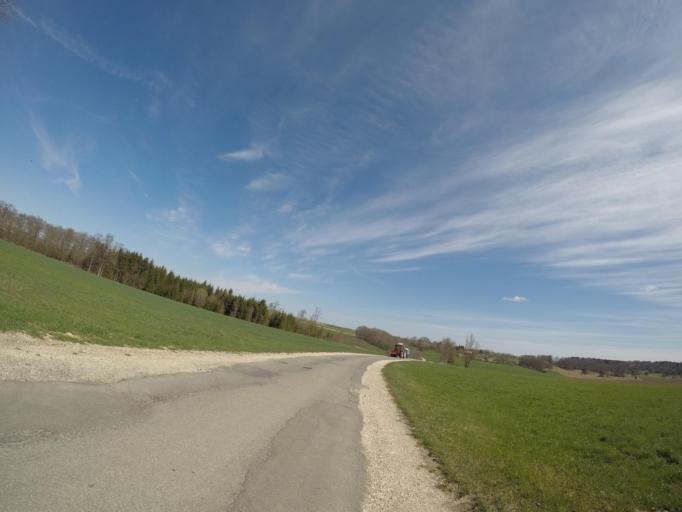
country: DE
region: Baden-Wuerttemberg
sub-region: Tuebingen Region
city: Mehrstetten
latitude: 48.3312
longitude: 9.5531
